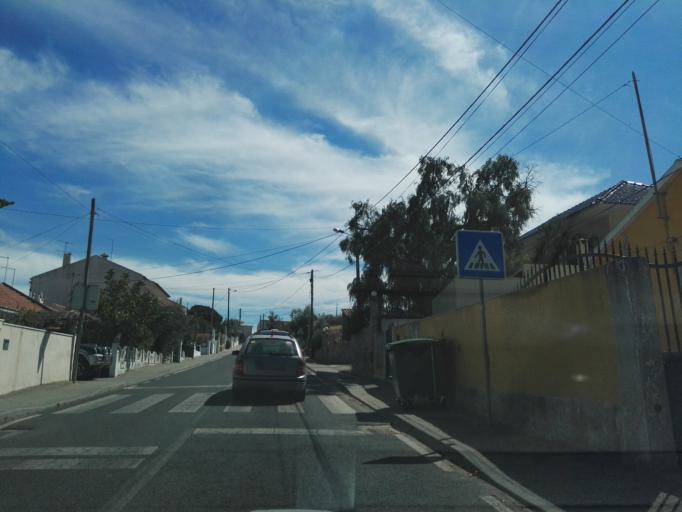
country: PT
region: Lisbon
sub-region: Arruda Dos Vinhos
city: Arruda dos Vinhos
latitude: 38.9625
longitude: -9.0614
